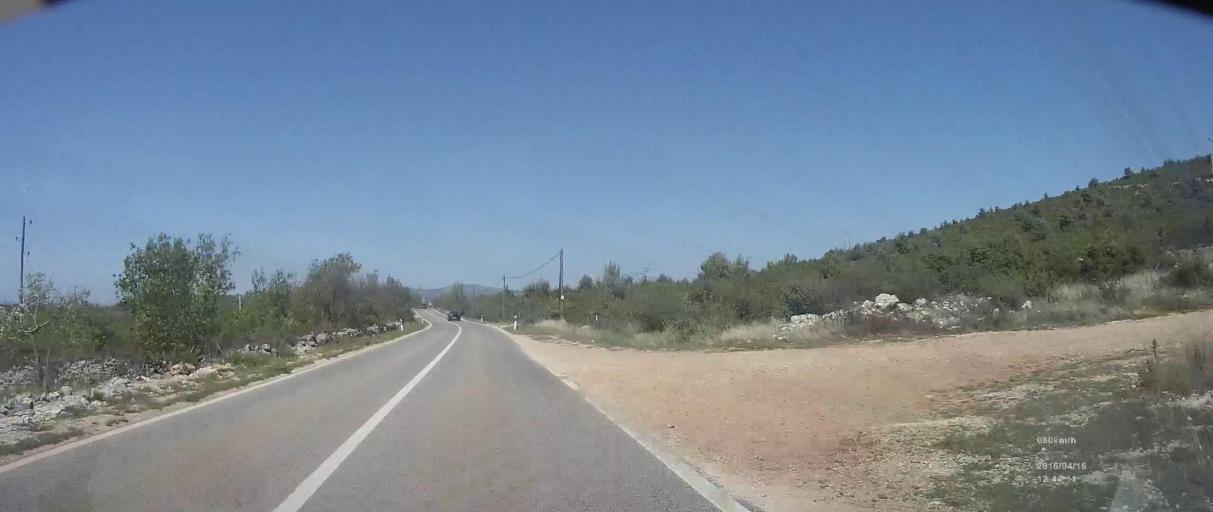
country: HR
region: Sibensko-Kniniska
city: Rogoznica
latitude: 43.6385
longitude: 16.0670
